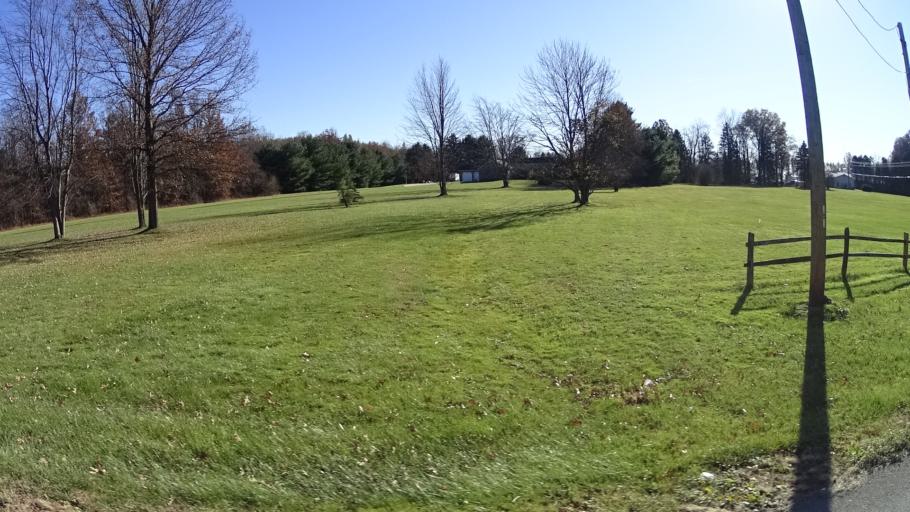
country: US
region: Ohio
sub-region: Lorain County
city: Elyria
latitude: 41.3174
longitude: -82.1104
